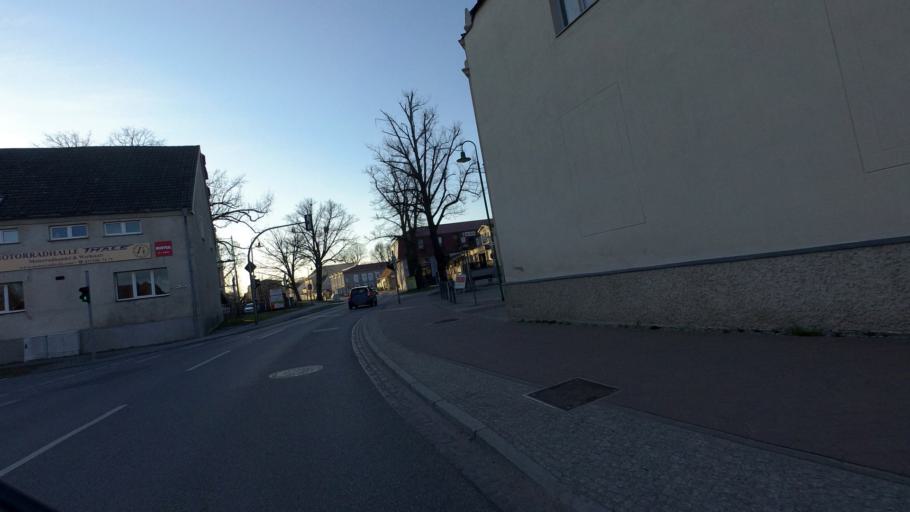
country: DE
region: Brandenburg
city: Werneuchen
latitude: 52.6302
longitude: 13.7328
